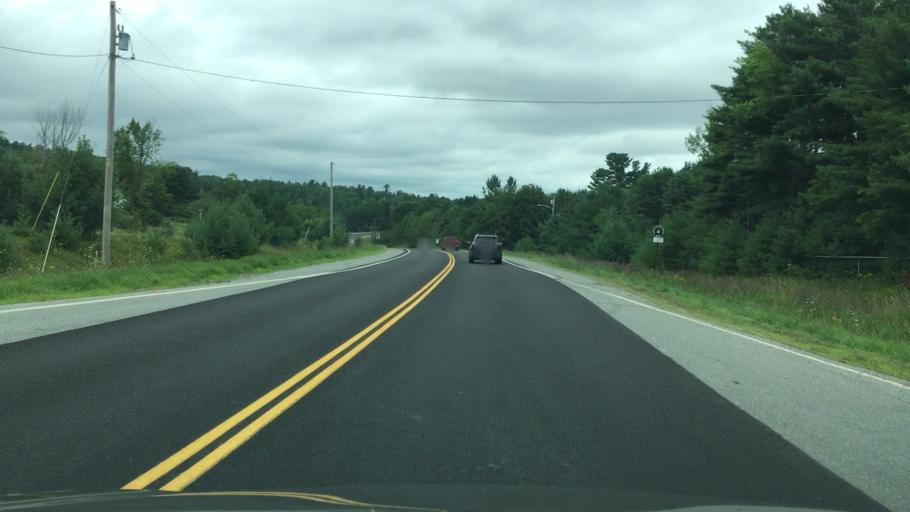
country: US
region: Maine
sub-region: Penobscot County
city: Orrington
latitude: 44.6949
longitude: -68.8142
